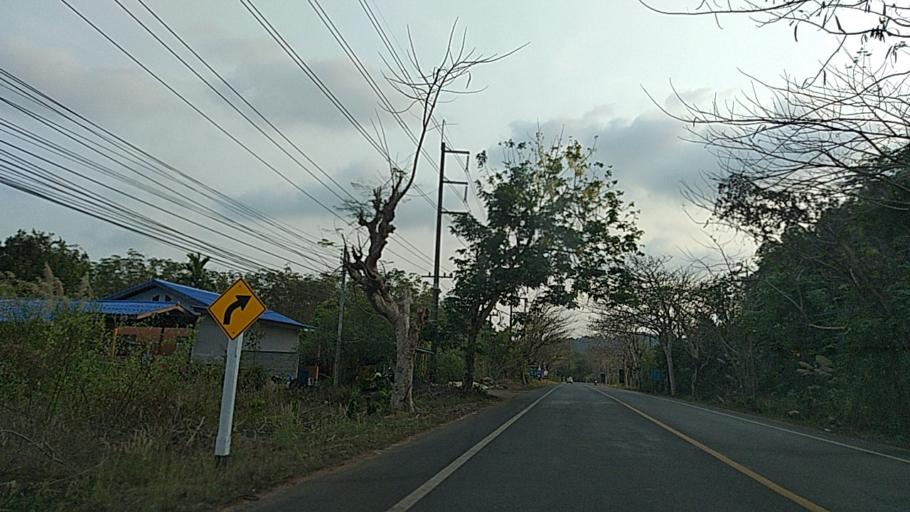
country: TH
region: Trat
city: Laem Ngop
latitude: 12.2833
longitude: 102.3102
